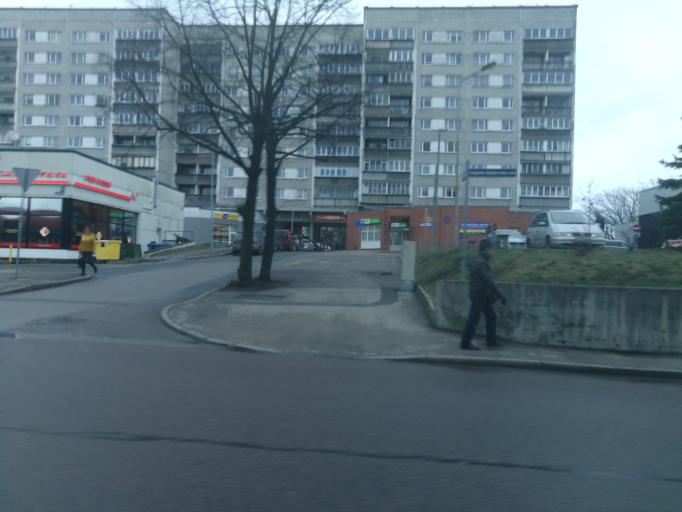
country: LV
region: Riga
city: Bolderaja
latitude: 57.0315
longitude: 24.1102
